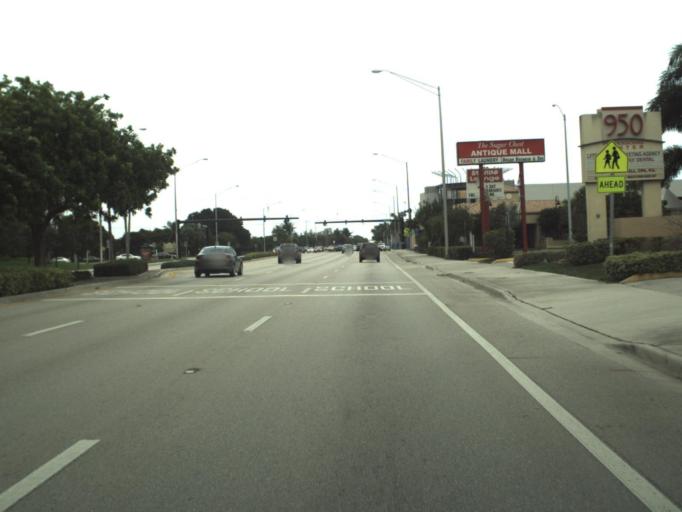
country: US
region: Florida
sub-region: Broward County
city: Pompano Beach
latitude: 26.2415
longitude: -80.1021
